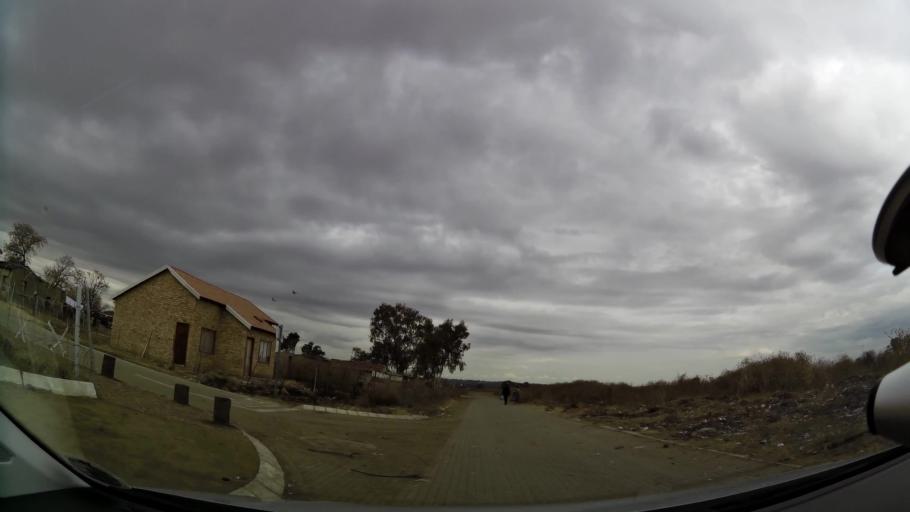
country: ZA
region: Orange Free State
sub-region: Fezile Dabi District Municipality
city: Kroonstad
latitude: -27.6489
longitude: 27.2144
